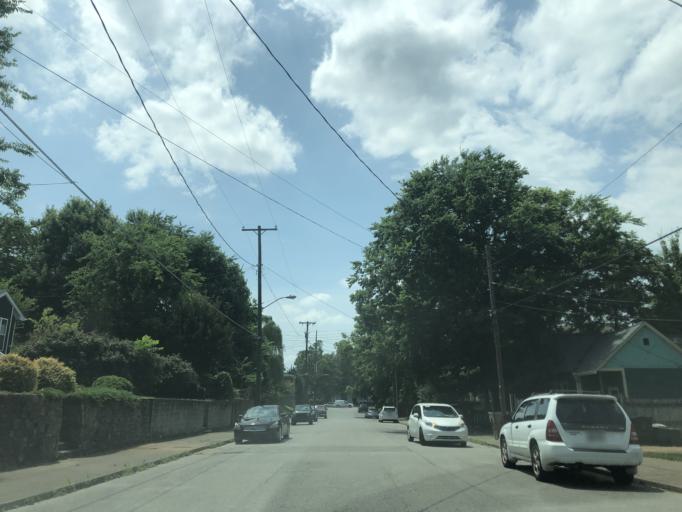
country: US
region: Tennessee
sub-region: Davidson County
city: Nashville
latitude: 36.1722
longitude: -86.7488
